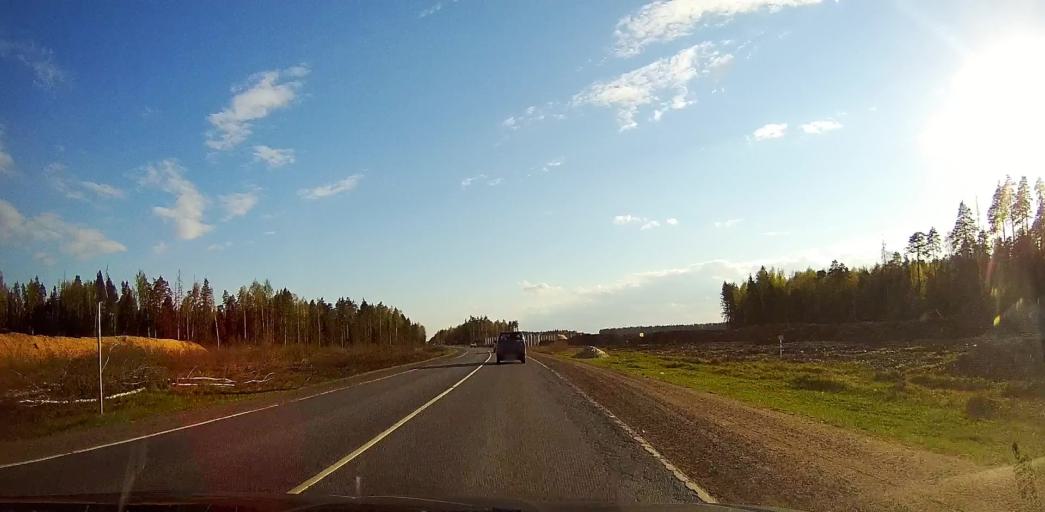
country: RU
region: Moskovskaya
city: Gzhel'
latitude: 55.6695
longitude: 38.3930
